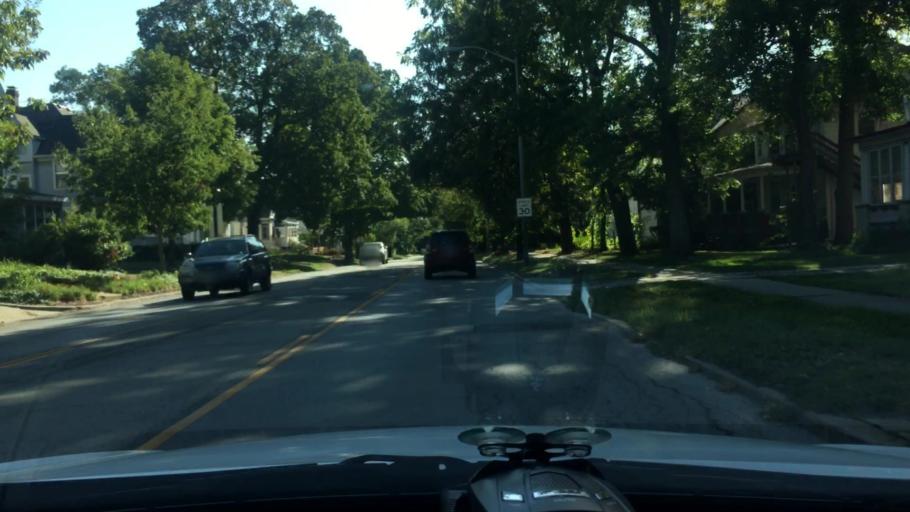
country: US
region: Illinois
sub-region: Champaign County
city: Champaign
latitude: 40.1126
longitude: -88.2539
